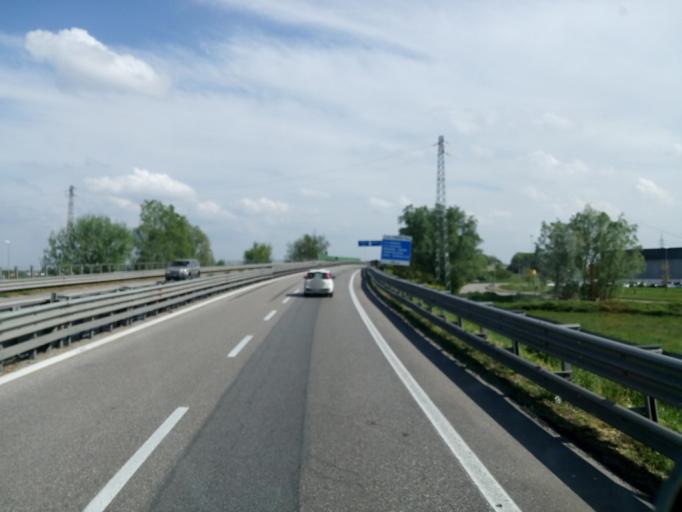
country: IT
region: Veneto
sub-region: Provincia di Verona
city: Legnago
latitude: 45.2006
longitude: 11.2596
